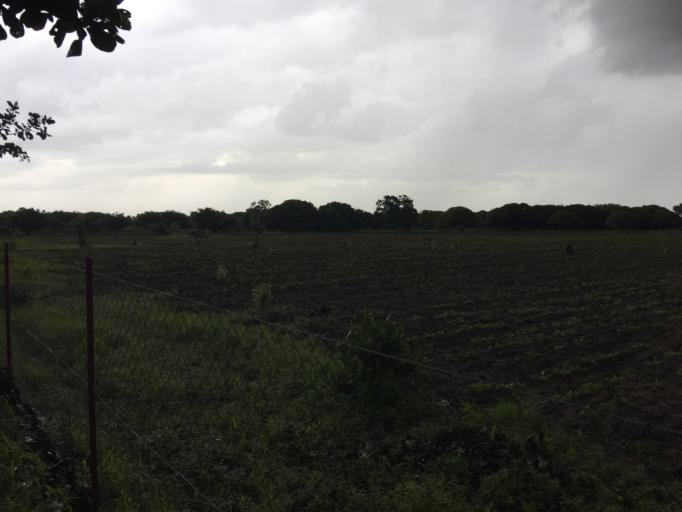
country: SN
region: Fatick
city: Sokone
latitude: 13.7539
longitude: -16.4339
